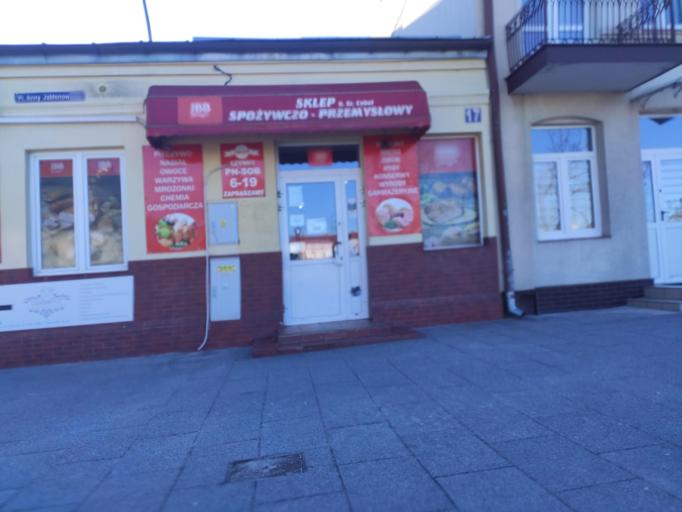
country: PL
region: Lublin Voivodeship
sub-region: Powiat lubartowski
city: Kock
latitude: 51.6380
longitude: 22.4471
